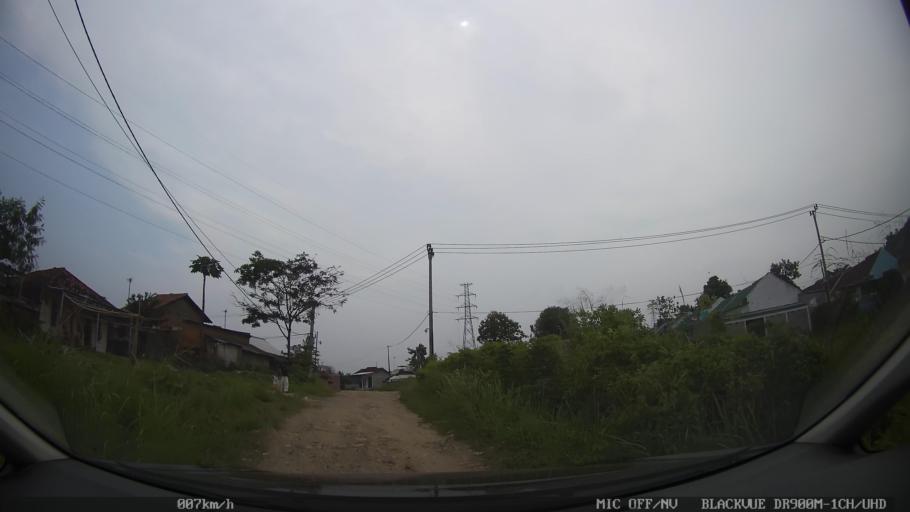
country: ID
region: Lampung
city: Panjang
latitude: -5.4262
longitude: 105.3424
